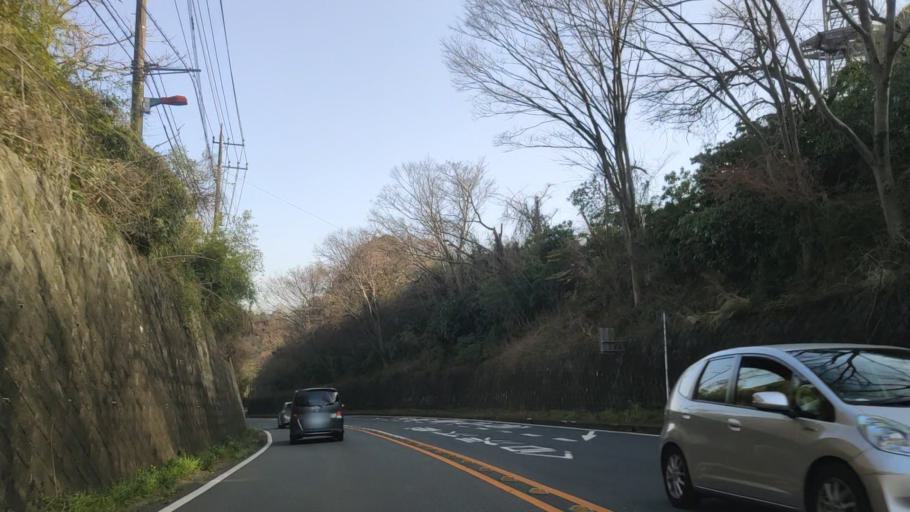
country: JP
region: Tokyo
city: Hachioji
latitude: 35.5524
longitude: 139.2631
